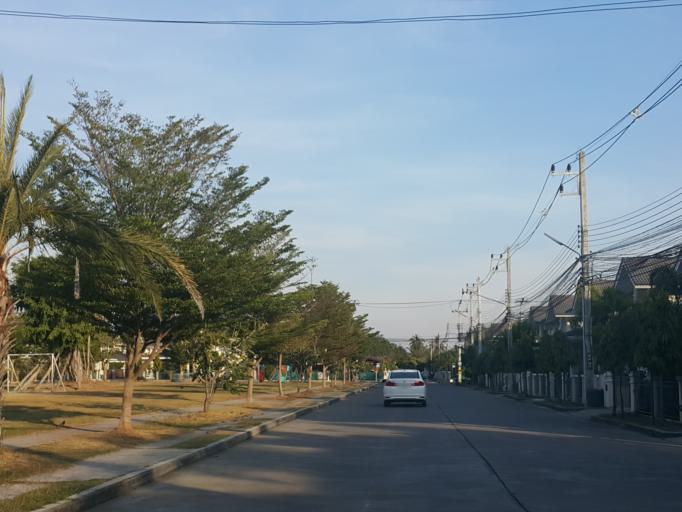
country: TH
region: Chiang Mai
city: San Sai
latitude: 18.8126
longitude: 99.0757
